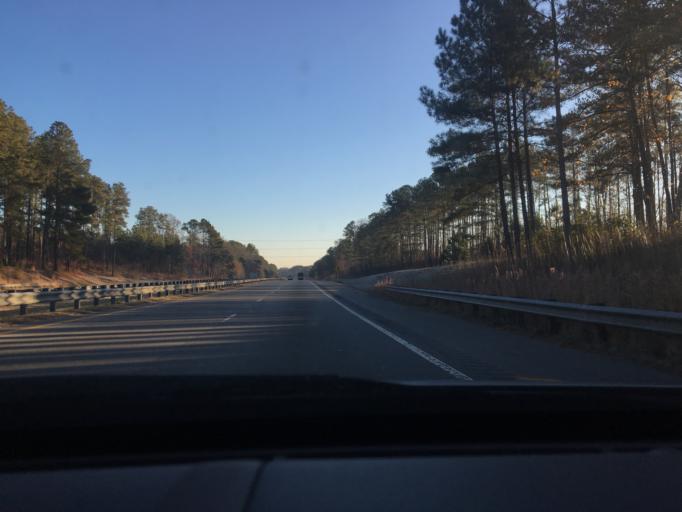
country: US
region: North Carolina
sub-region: Wake County
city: Holly Springs
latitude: 35.6687
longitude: -78.9309
